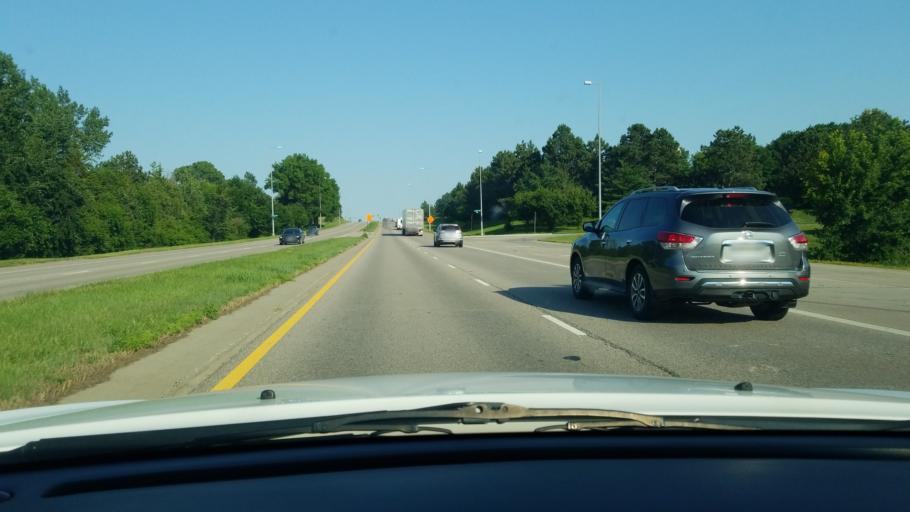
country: US
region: Nebraska
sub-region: Lancaster County
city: Lincoln
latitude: 40.7490
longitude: -96.6307
